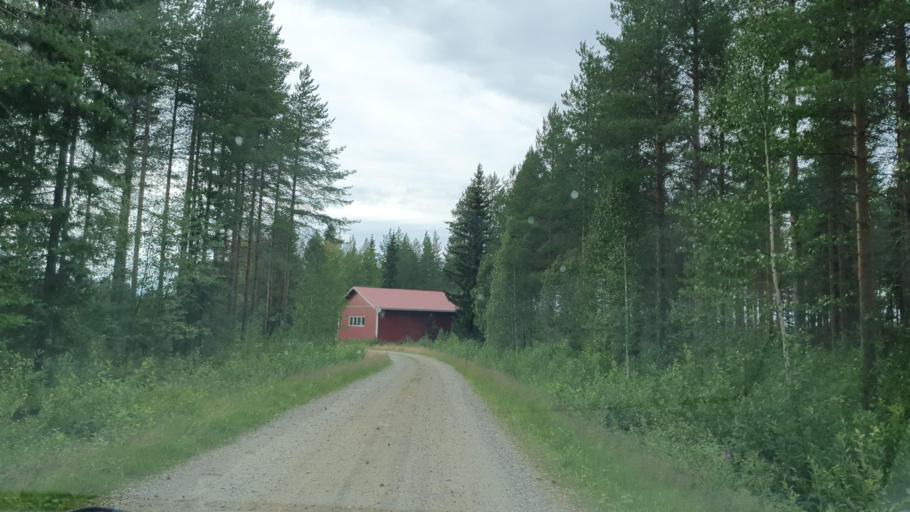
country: FI
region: Kainuu
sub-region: Kehys-Kainuu
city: Kuhmo
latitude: 64.2033
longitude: 29.3810
